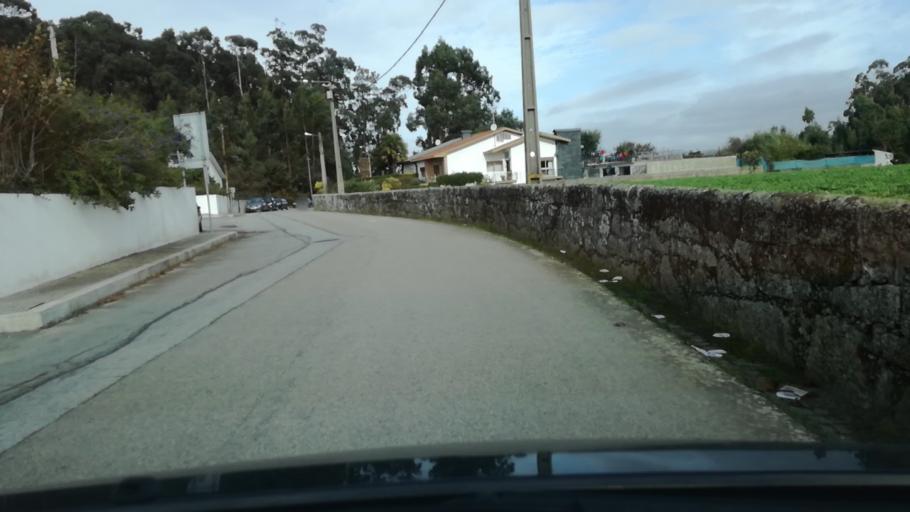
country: PT
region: Porto
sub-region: Maia
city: Gemunde
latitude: 41.2607
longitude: -8.6746
